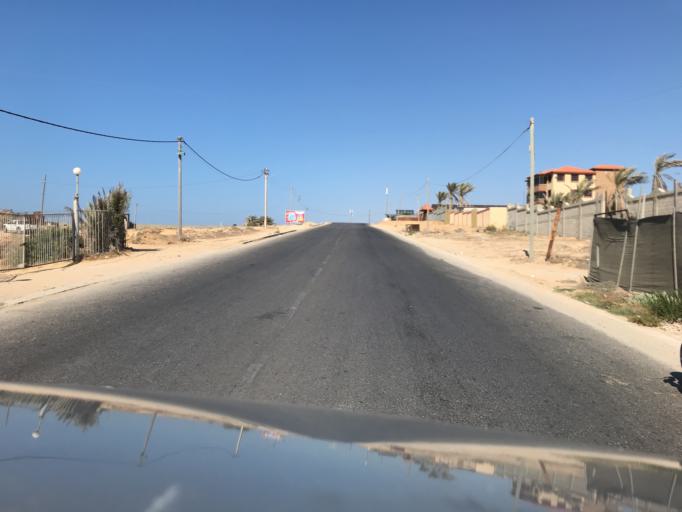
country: PS
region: Gaza Strip
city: Az Zuwaydah
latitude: 31.4551
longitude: 34.3684
